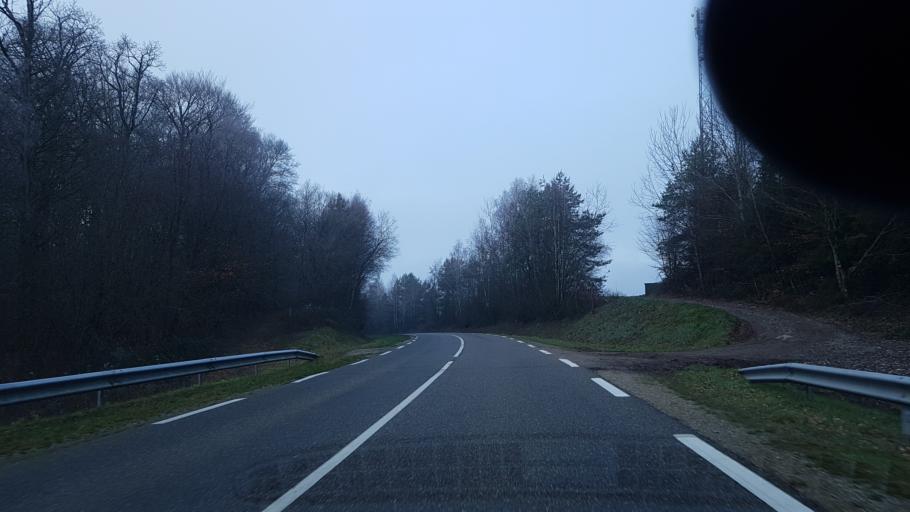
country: FR
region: Lorraine
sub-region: Departement de la Moselle
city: Bitche
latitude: 49.0451
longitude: 7.4081
